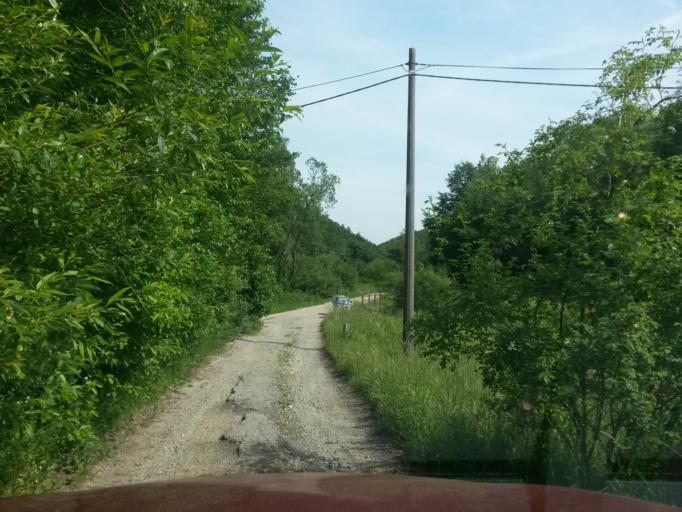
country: SK
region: Kosicky
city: Kosice
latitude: 48.7376
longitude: 21.1170
